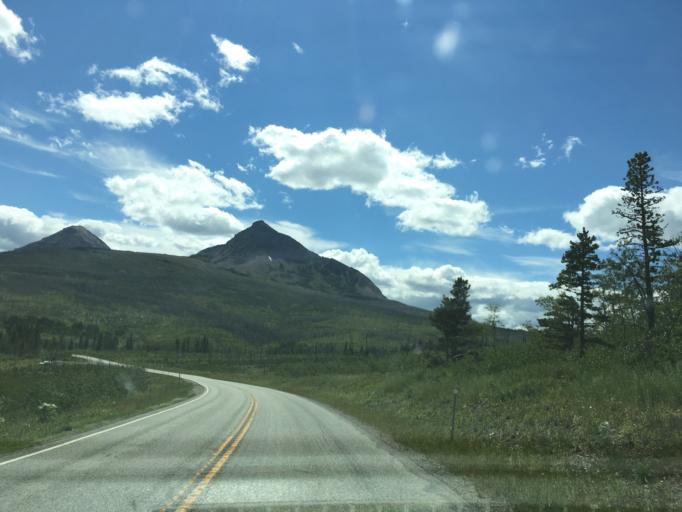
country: US
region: Montana
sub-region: Glacier County
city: North Browning
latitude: 48.6857
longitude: -113.3543
